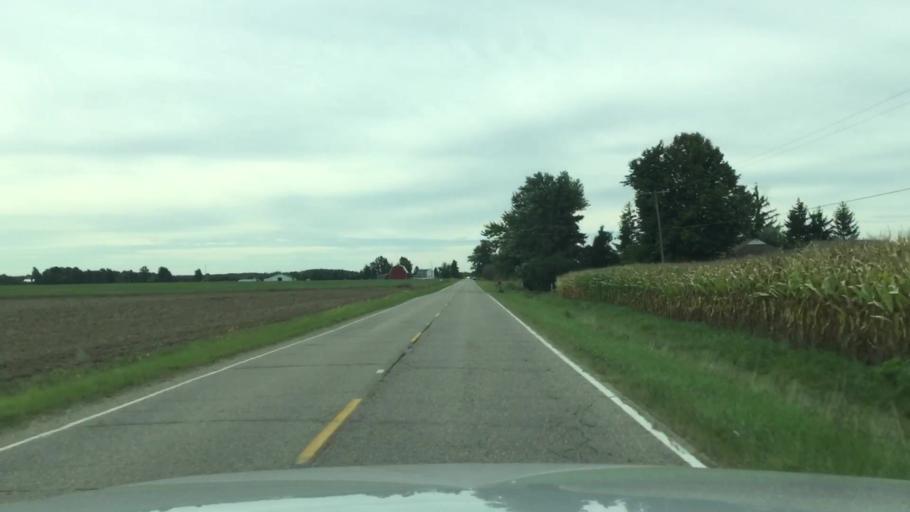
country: US
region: Michigan
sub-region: Genesee County
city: Montrose
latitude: 43.0849
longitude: -83.9878
